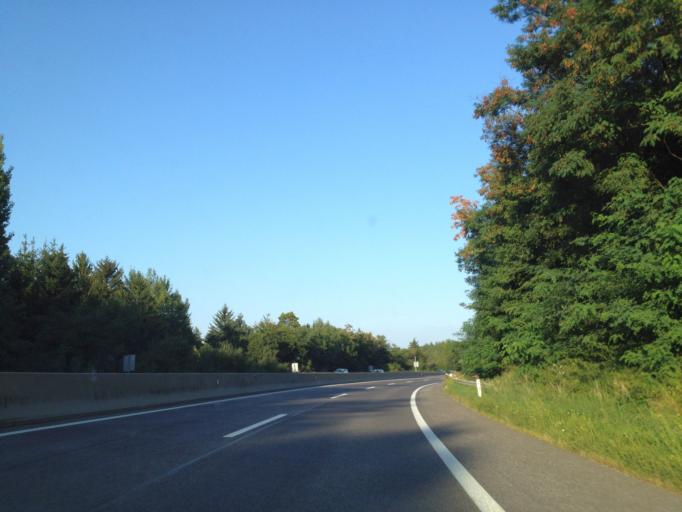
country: AT
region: Lower Austria
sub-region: Politischer Bezirk Neunkirchen
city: Wimpassing im Schwarzatale
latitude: 47.6789
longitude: 16.0181
